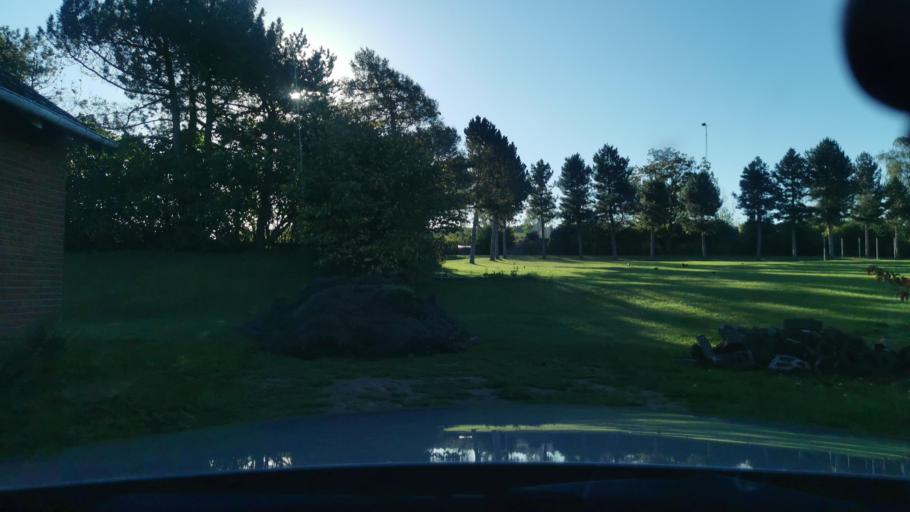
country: DK
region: Zealand
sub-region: Kalundborg Kommune
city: Svebolle
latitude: 55.6496
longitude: 11.2857
